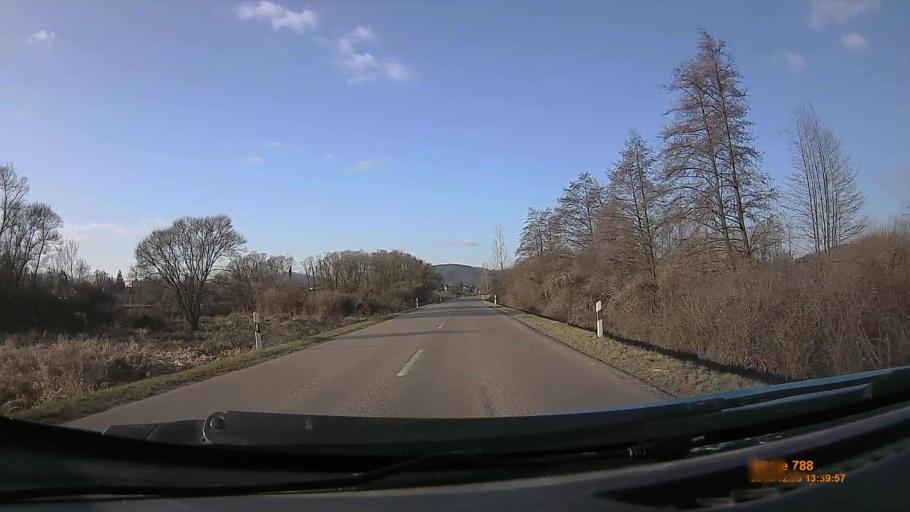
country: HU
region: Heves
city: Recsk
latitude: 47.9275
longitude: 20.1301
